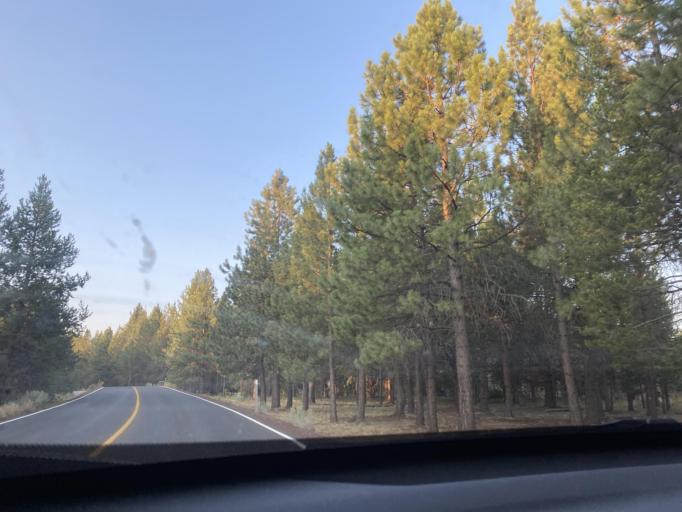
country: US
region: Oregon
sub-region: Deschutes County
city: Sunriver
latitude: 43.8847
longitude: -121.4400
